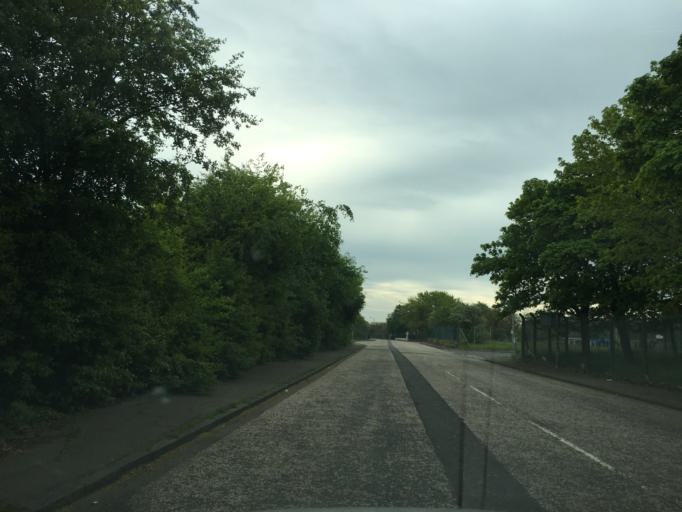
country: GB
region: Scotland
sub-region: Edinburgh
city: Ratho
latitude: 55.9521
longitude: -3.3490
